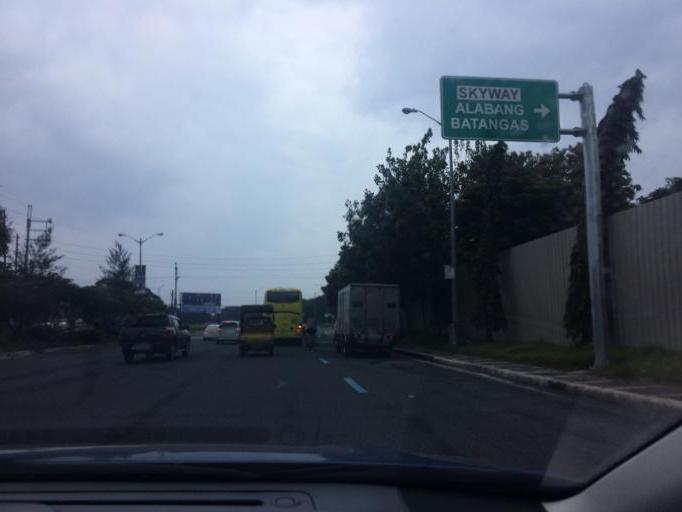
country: PH
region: Metro Manila
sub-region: City of Manila
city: Port Area
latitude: 14.5502
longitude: 120.9863
